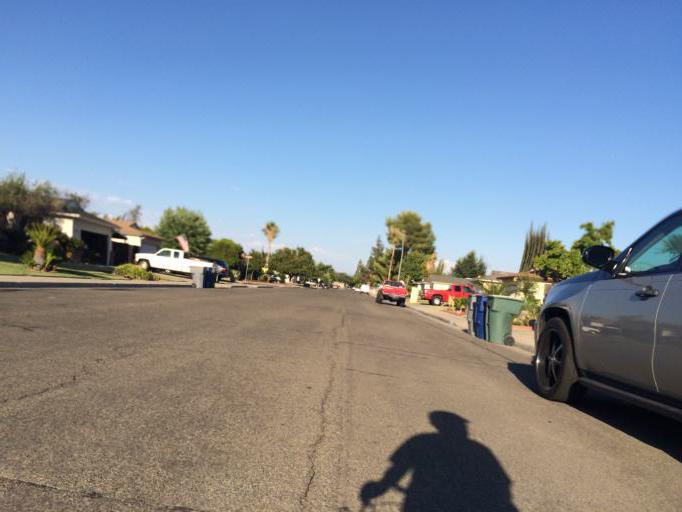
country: US
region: California
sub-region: Fresno County
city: Tarpey Village
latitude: 36.8038
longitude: -119.6884
